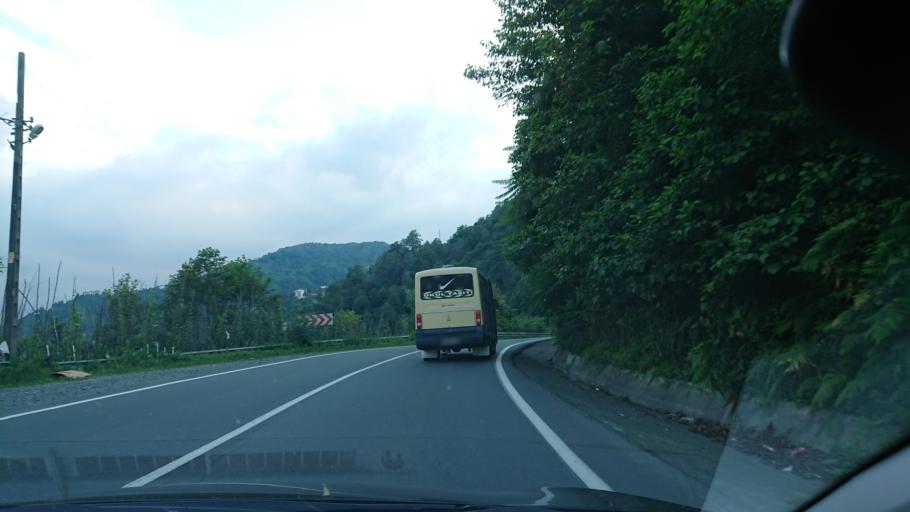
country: TR
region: Rize
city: Cayeli
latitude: 41.0776
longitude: 40.7132
